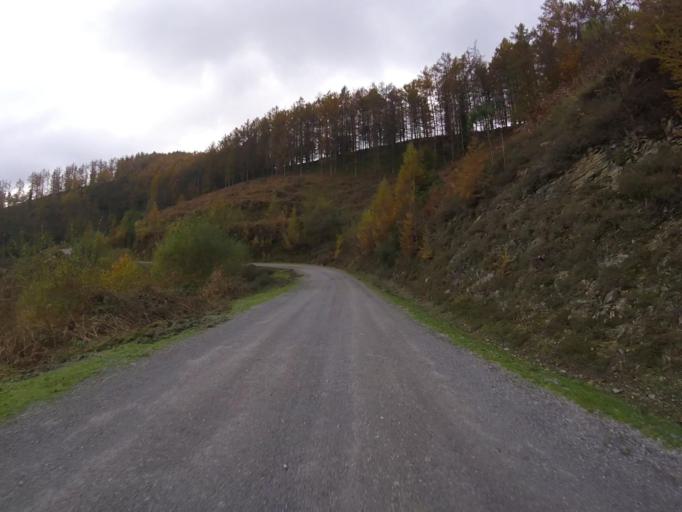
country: ES
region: Navarre
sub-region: Provincia de Navarra
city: Goizueta
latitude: 43.2188
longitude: -1.8227
